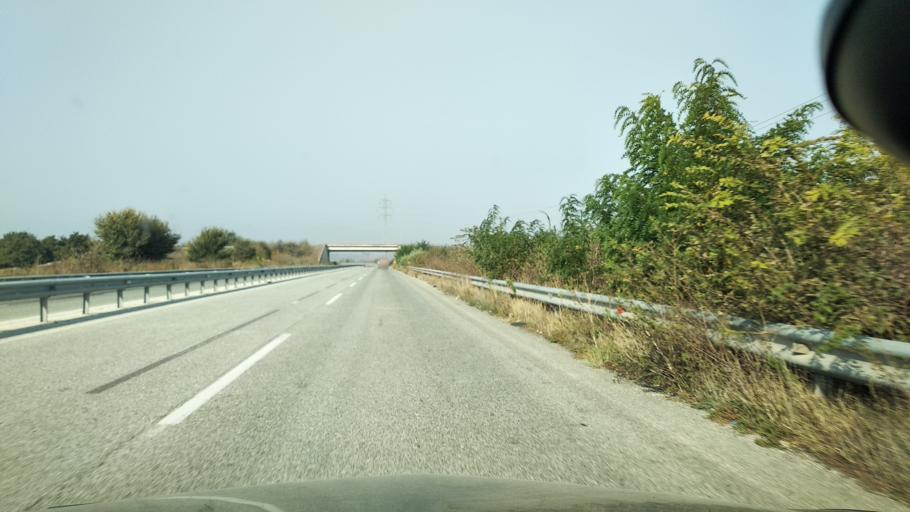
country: GR
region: Thessaly
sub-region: Trikala
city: Megalochori
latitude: 39.5653
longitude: 21.8488
